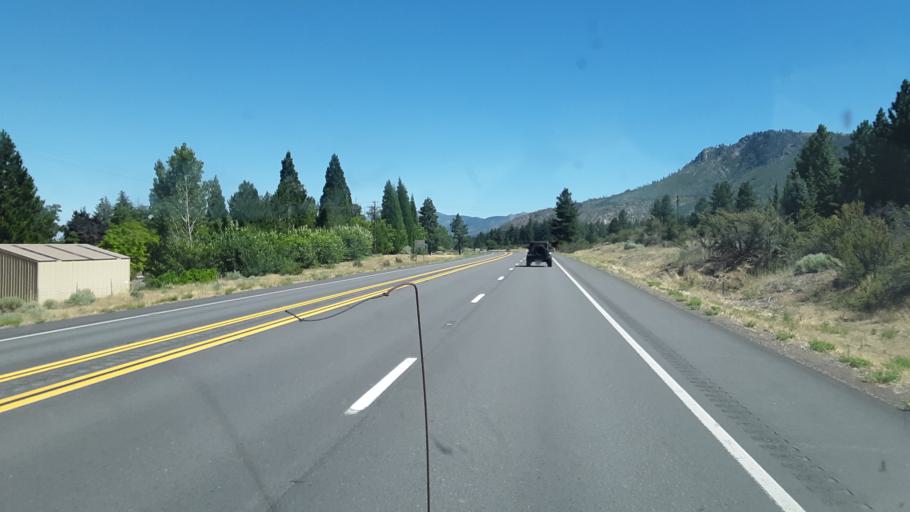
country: US
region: California
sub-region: Lassen County
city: Janesville
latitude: 40.2502
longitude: -120.4619
